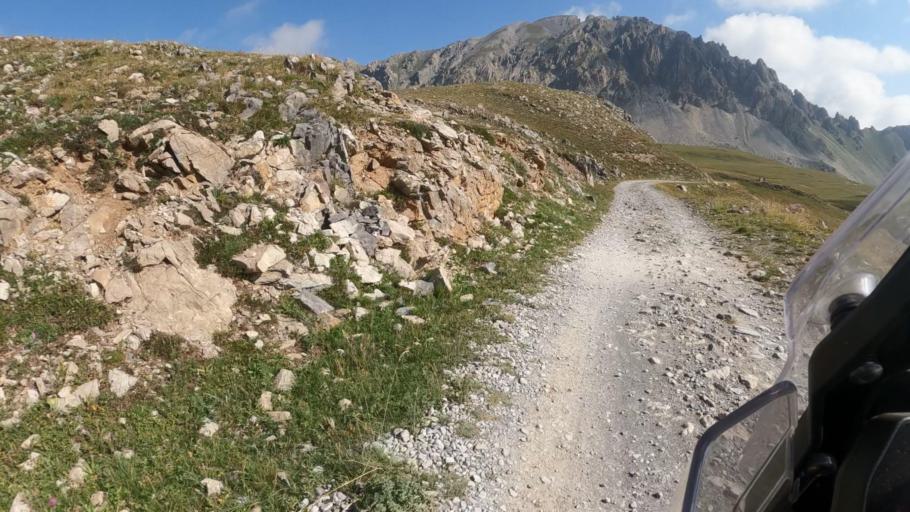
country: IT
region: Piedmont
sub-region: Provincia di Cuneo
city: Bersezio
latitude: 44.4035
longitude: 7.0156
